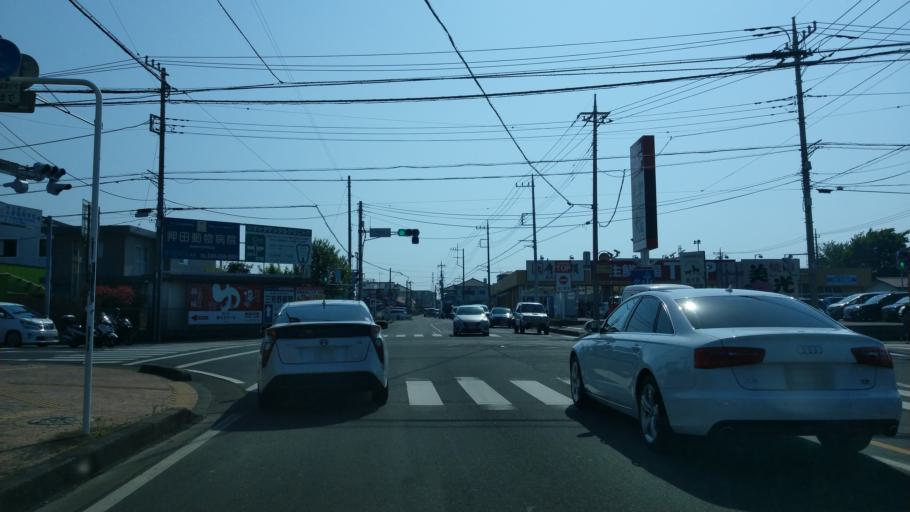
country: JP
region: Saitama
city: Oi
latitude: 35.8541
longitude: 139.5162
